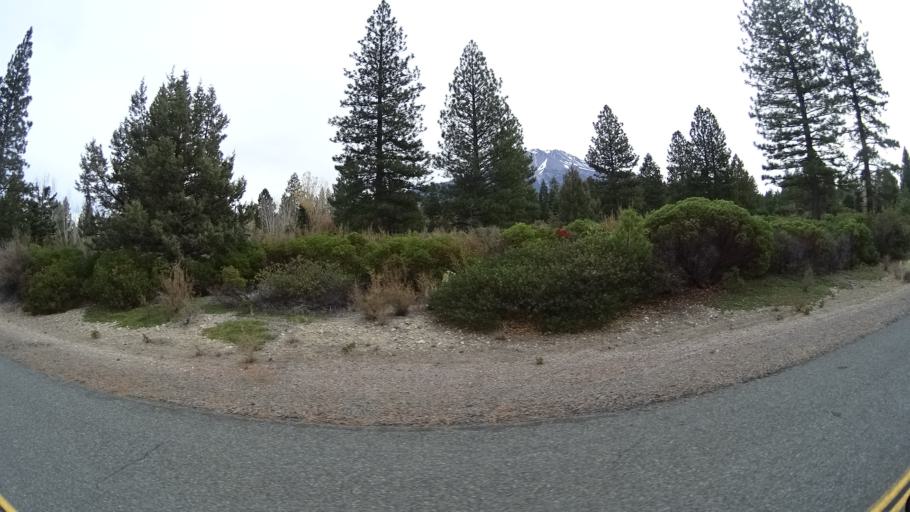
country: US
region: California
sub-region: Siskiyou County
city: Weed
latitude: 41.4107
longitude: -122.3649
